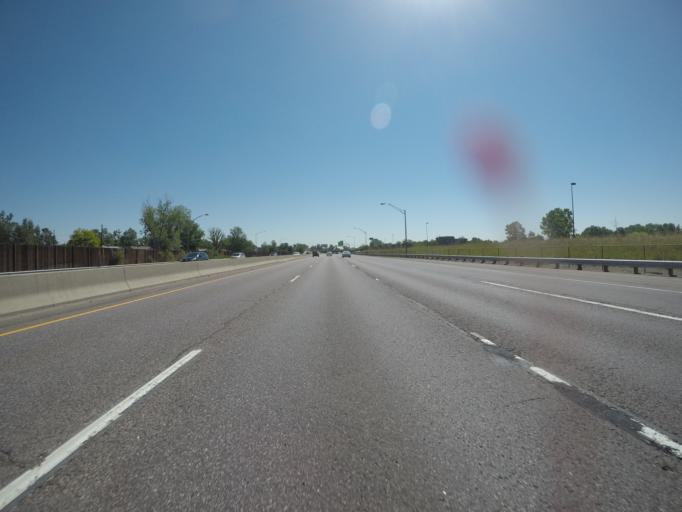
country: US
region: Colorado
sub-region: Adams County
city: Berkley
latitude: 39.7835
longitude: -105.0310
